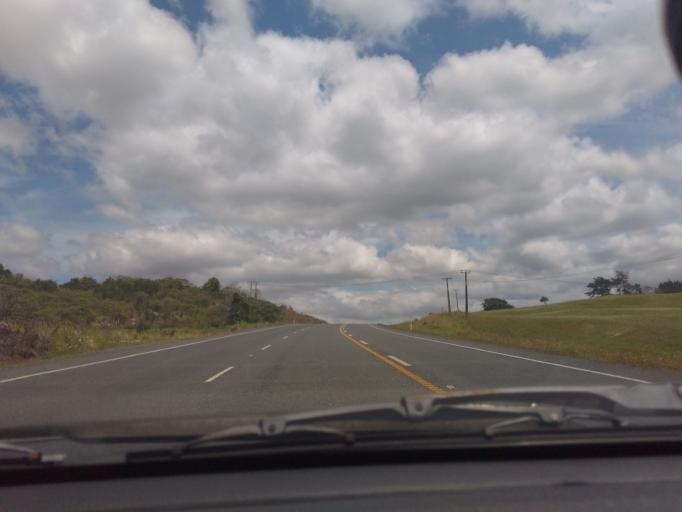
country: NZ
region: Northland
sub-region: Far North District
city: Moerewa
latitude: -35.3600
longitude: 173.9659
